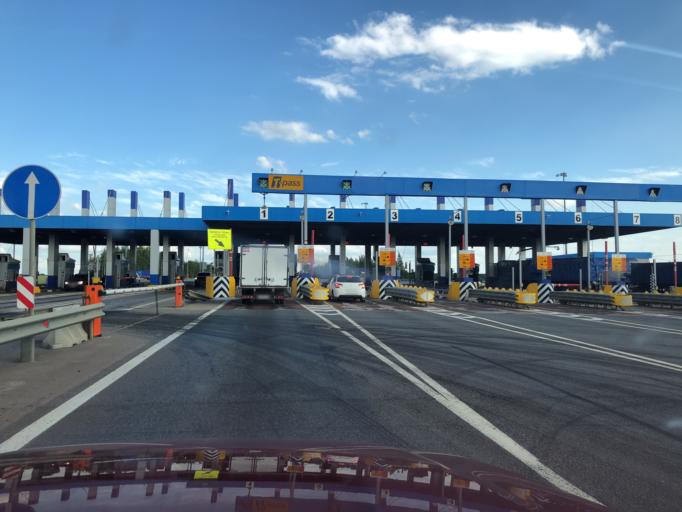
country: RU
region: Lipetsk
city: Zadonsk
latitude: 52.4305
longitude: 38.8241
